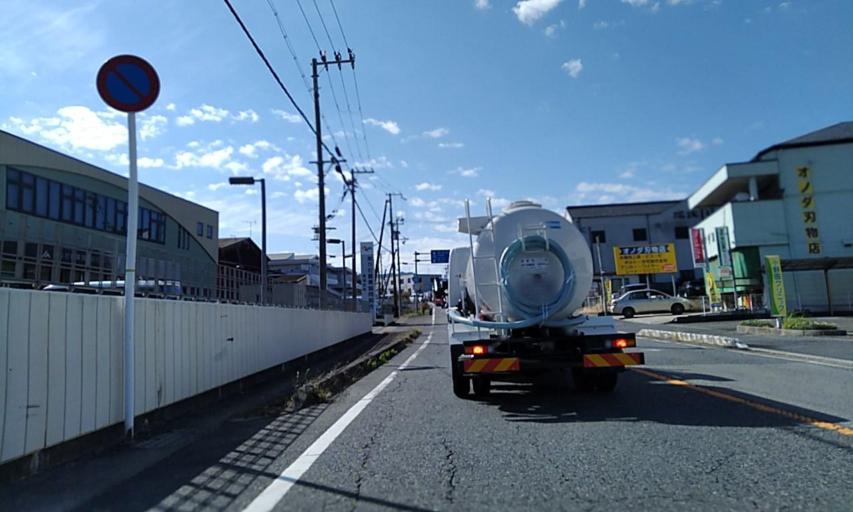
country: JP
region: Wakayama
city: Kainan
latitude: 34.0385
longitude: 135.1858
